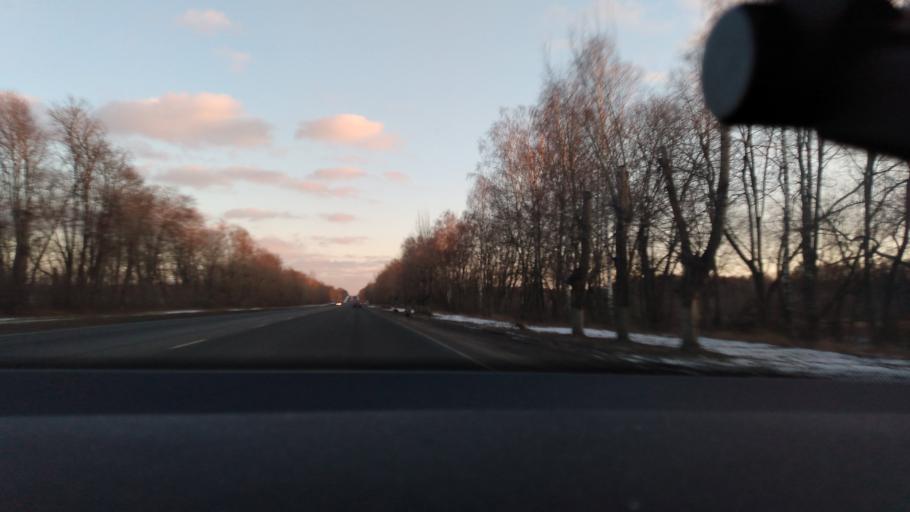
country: RU
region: Moskovskaya
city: Raduzhnyy
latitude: 55.1875
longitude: 38.6372
